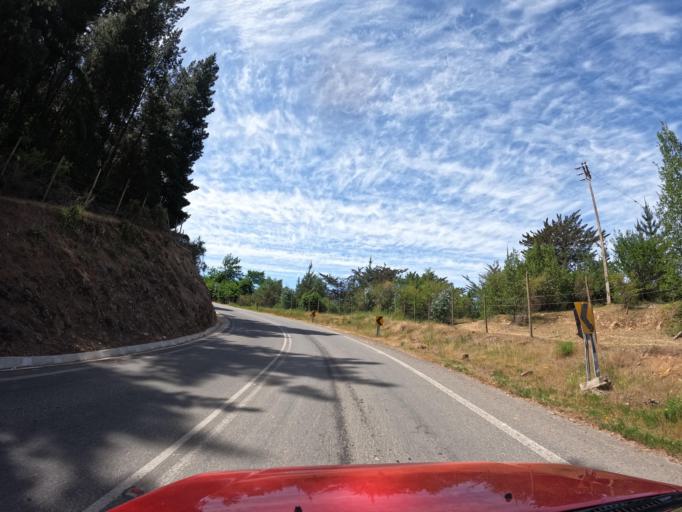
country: CL
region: Maule
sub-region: Provincia de Talca
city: Talca
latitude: -34.9953
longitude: -71.8091
